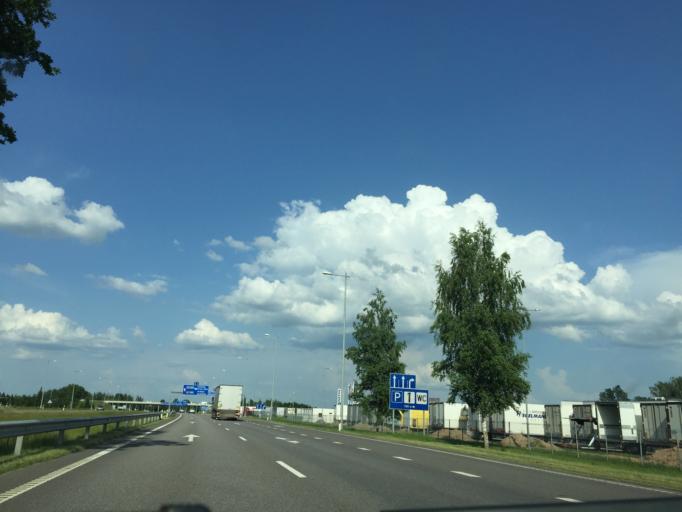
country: LT
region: Kauno apskritis
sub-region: Kauno rajonas
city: Garliava
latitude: 54.8093
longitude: 23.8570
